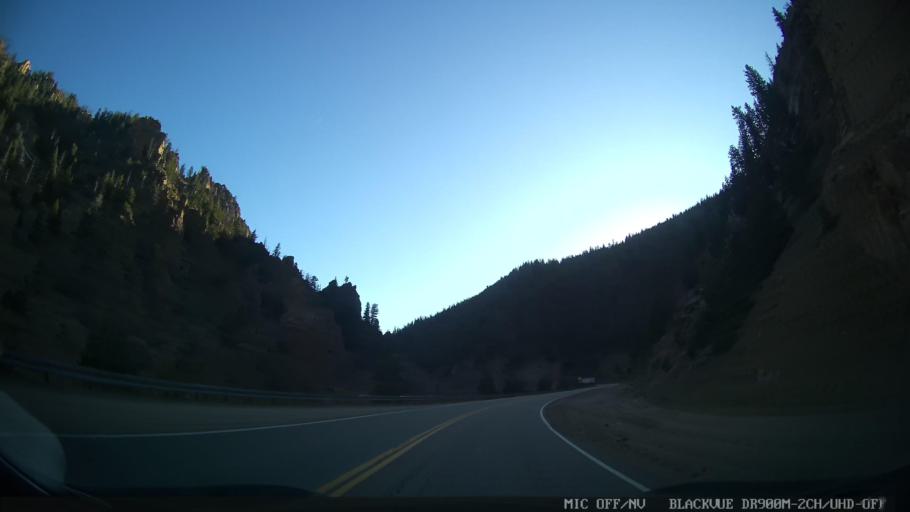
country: US
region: Colorado
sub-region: Grand County
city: Hot Sulphur Springs
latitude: 40.0620
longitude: -106.1289
